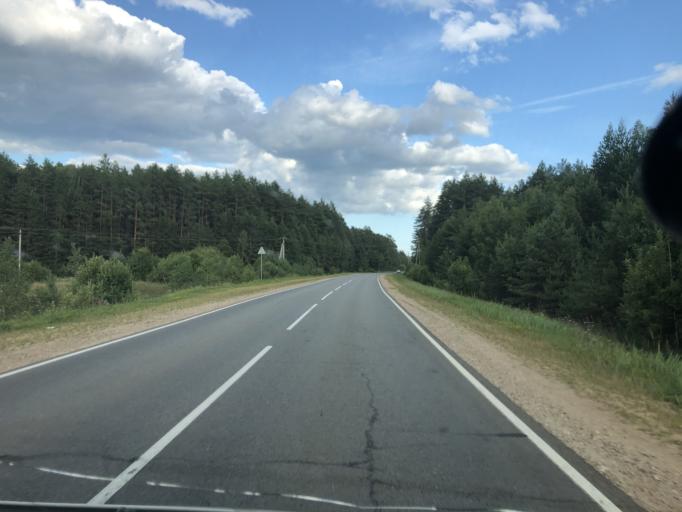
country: RU
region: Kaluga
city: Yukhnov
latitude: 54.7232
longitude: 35.2150
